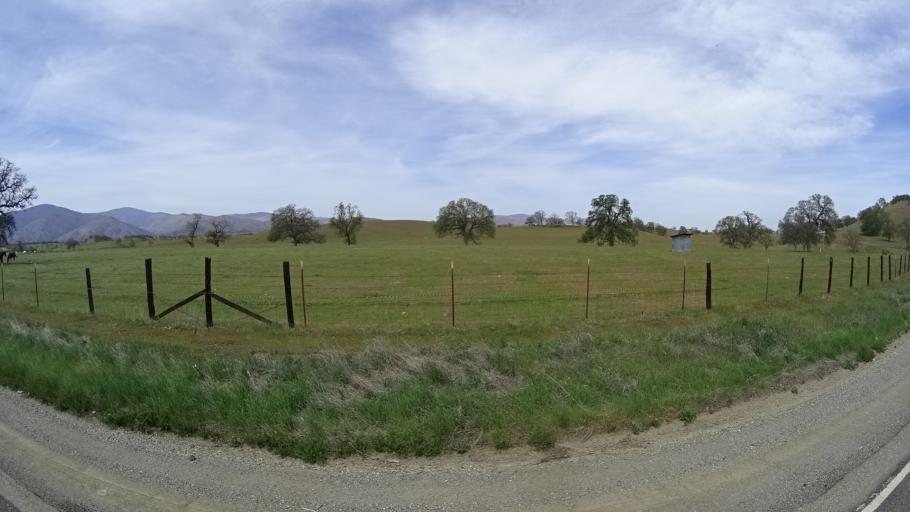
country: US
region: California
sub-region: Glenn County
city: Willows
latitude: 39.6106
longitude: -122.5309
